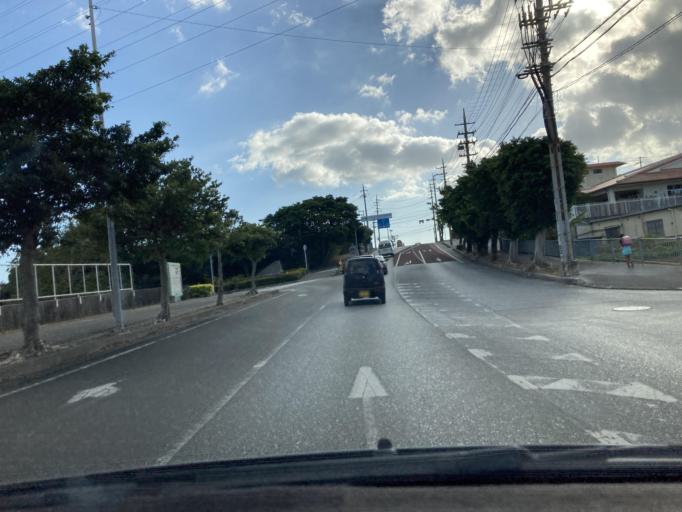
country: JP
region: Okinawa
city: Gushikawa
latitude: 26.3576
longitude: 127.8495
